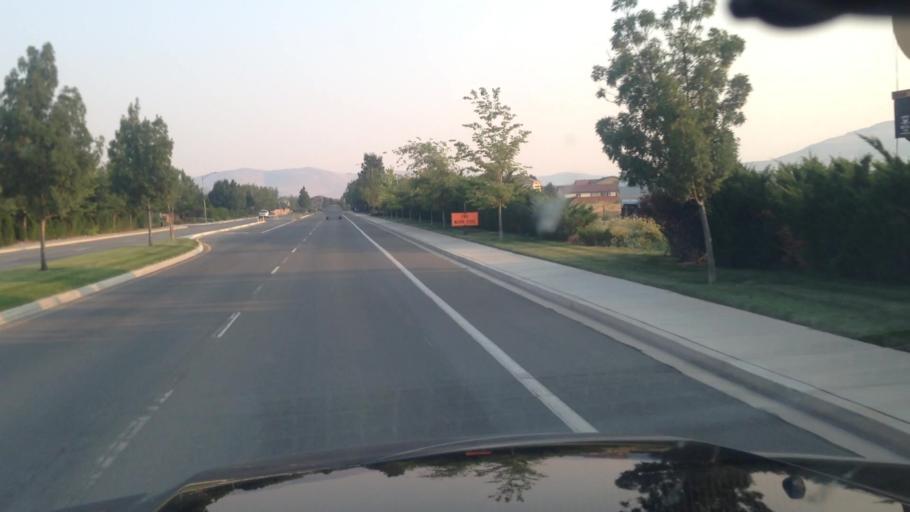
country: US
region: Nevada
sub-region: Washoe County
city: Sparks
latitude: 39.4111
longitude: -119.7335
